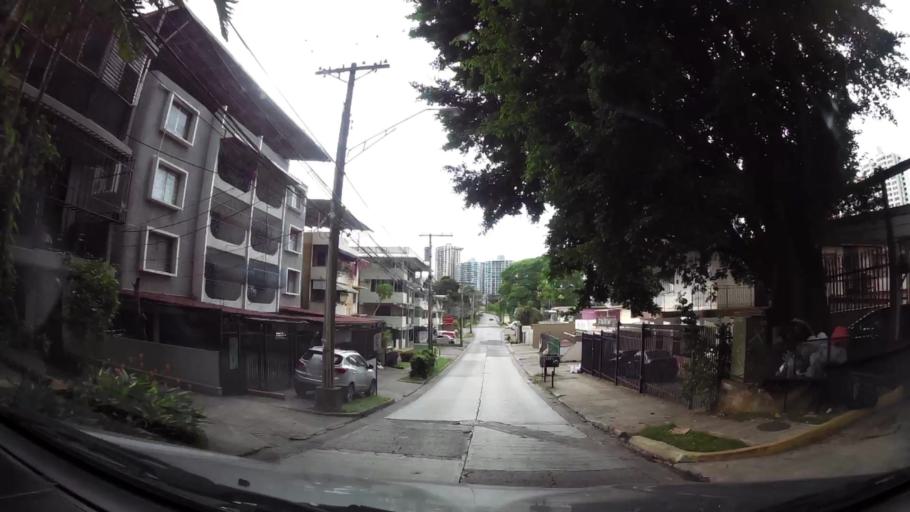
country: PA
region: Panama
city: Panama
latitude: 8.9826
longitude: -79.5180
